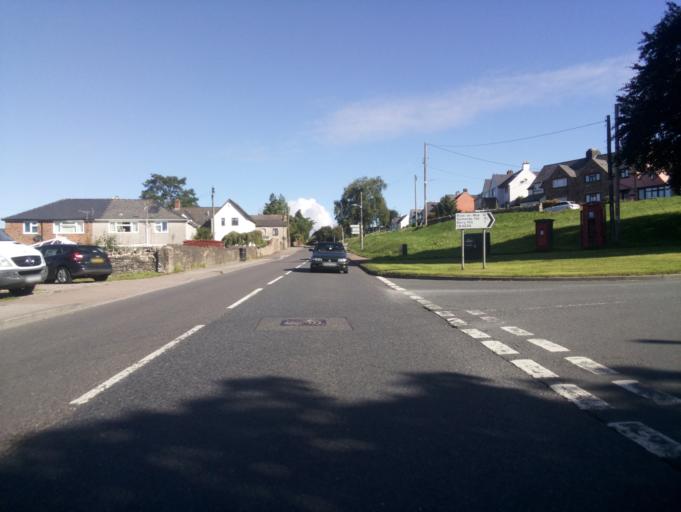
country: GB
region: England
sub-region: Gloucestershire
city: Coleford
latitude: 51.7962
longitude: -2.6198
